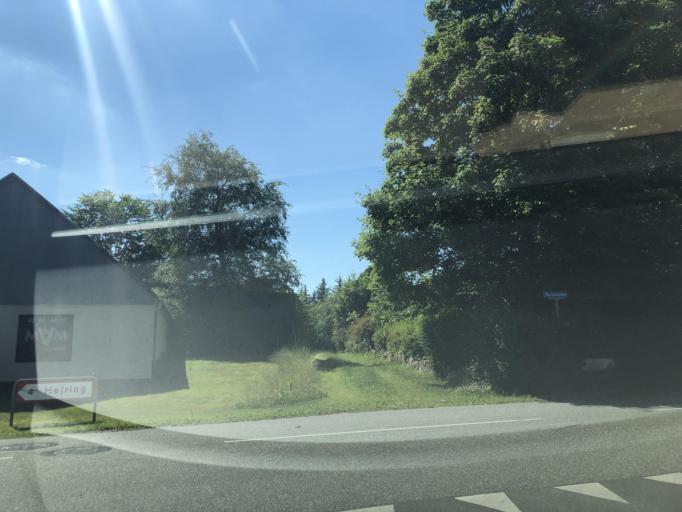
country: DK
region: North Denmark
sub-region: Mariagerfjord Kommune
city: Hobro
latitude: 56.6233
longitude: 9.6992
